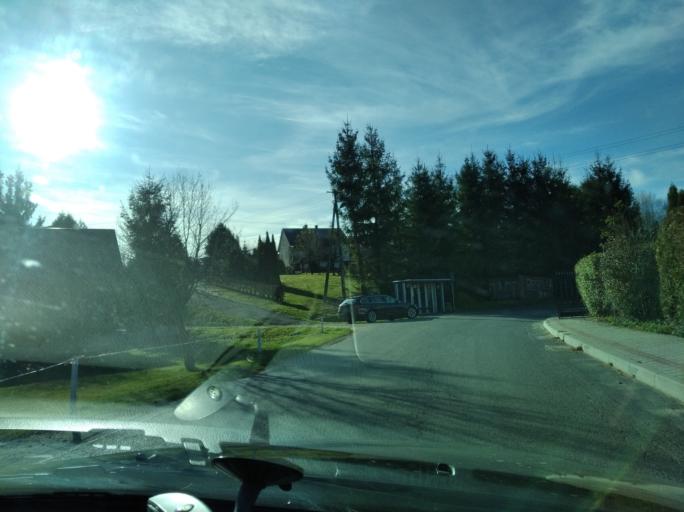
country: PL
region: Subcarpathian Voivodeship
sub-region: Powiat rzeszowski
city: Lutoryz
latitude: 49.9663
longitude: 21.9032
